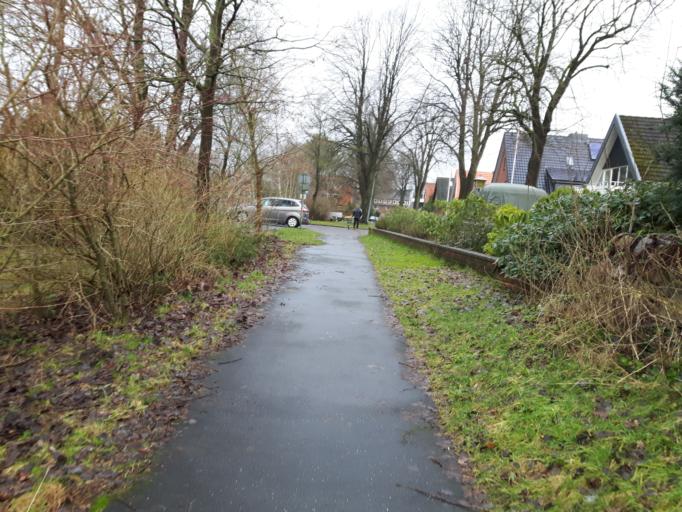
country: DE
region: Schleswig-Holstein
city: Westerronfeld
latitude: 54.2913
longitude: 9.6562
